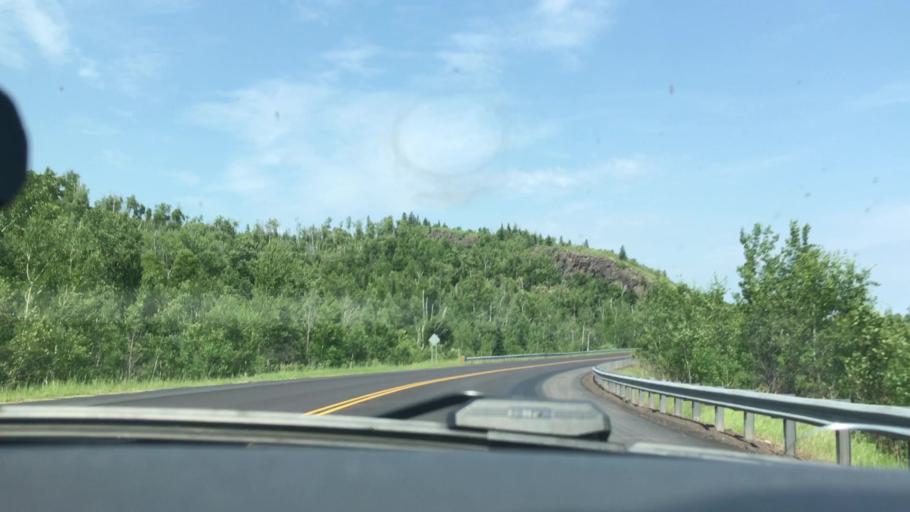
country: US
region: Minnesota
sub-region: Lake County
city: Silver Bay
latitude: 47.3754
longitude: -91.1636
